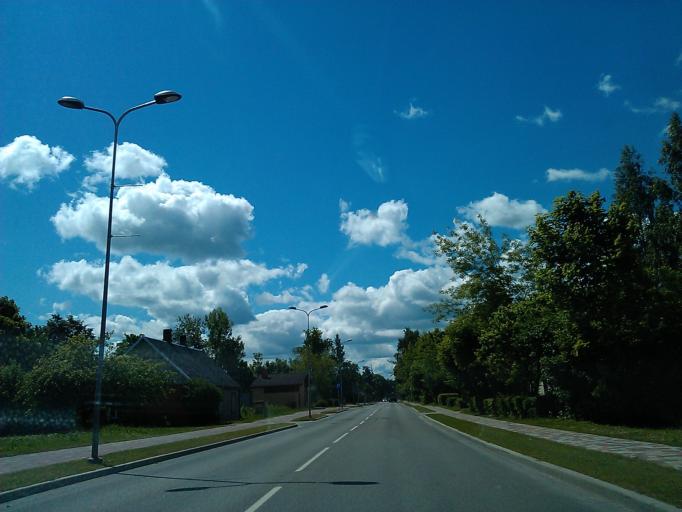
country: LV
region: Vilanu
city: Vilani
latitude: 56.5595
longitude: 26.9258
